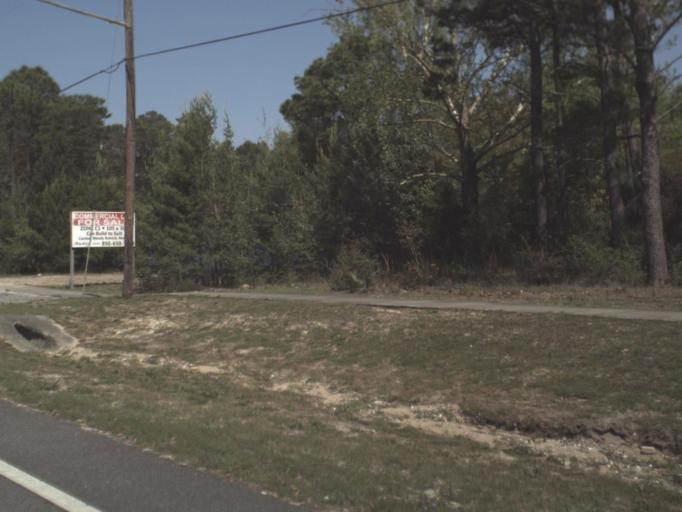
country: US
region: Florida
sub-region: Okaloosa County
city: Valparaiso
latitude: 30.5101
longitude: -86.5003
